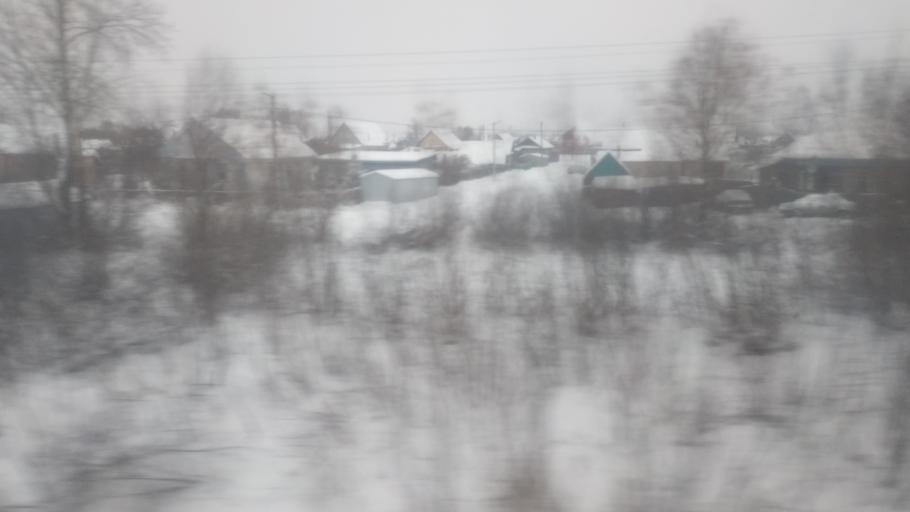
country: RU
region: Bashkortostan
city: Yanaul
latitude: 56.2788
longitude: 54.9516
